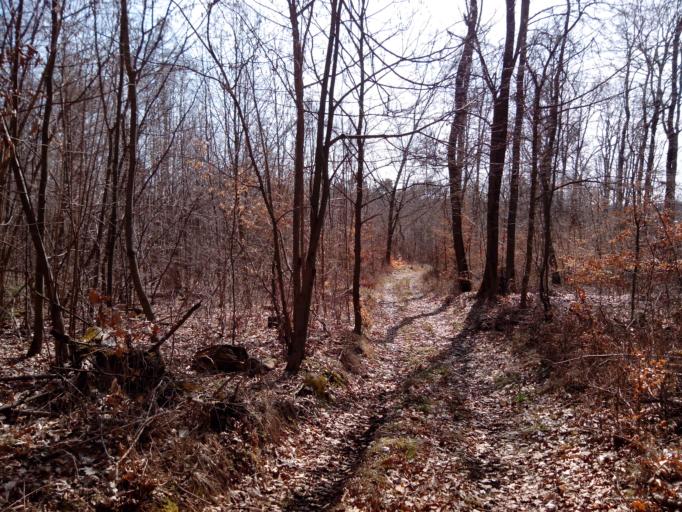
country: CZ
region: Central Bohemia
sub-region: Okres Beroun
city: Beroun
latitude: 49.9366
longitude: 14.1071
